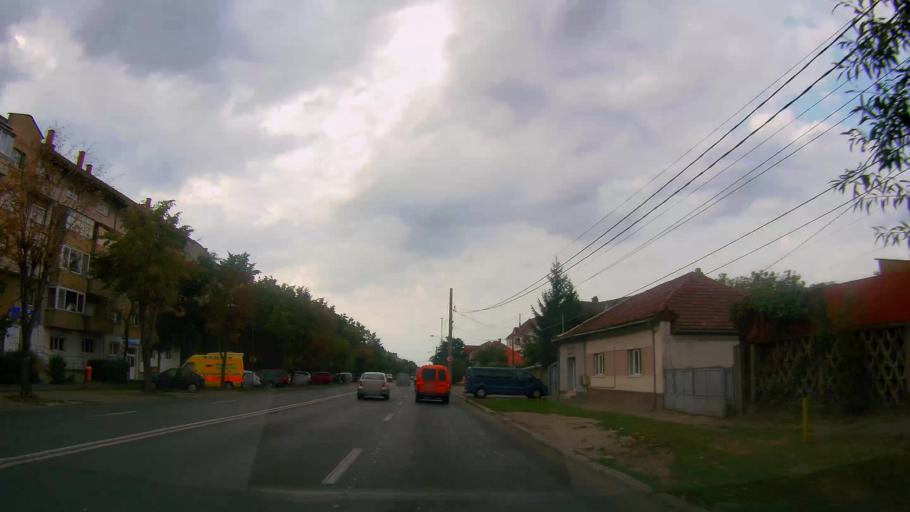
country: RO
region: Satu Mare
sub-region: Municipiul Satu Mare
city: Satu Mare
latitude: 47.7748
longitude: 22.8838
